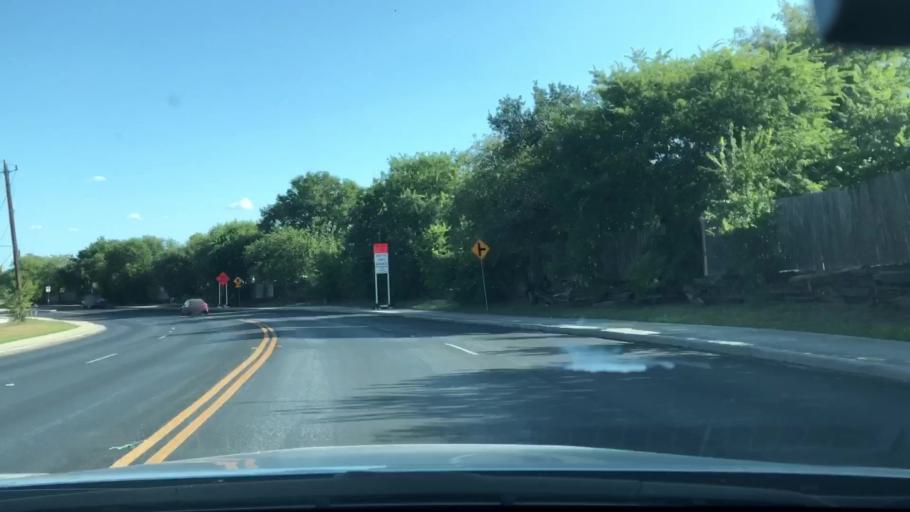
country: US
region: Texas
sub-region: Bexar County
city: Kirby
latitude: 29.4792
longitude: -98.3486
